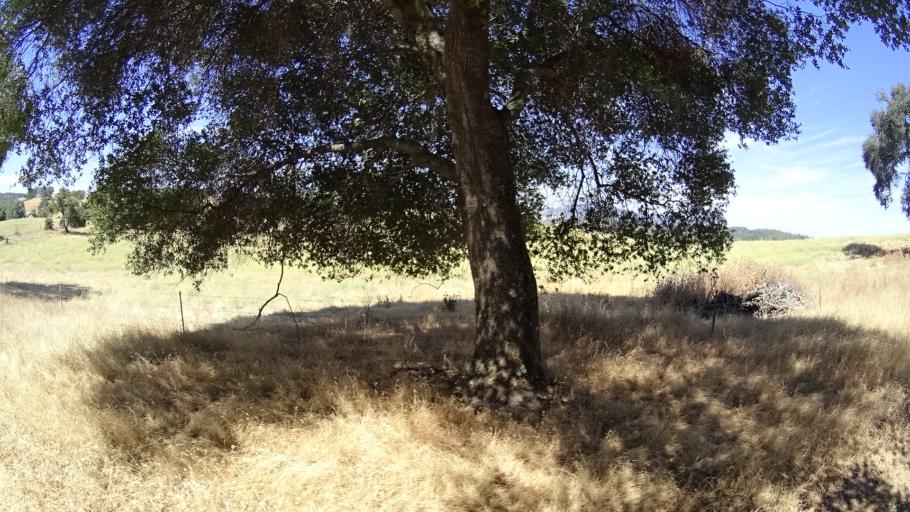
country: US
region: California
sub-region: Calaveras County
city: Angels Camp
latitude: 38.1160
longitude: -120.5683
